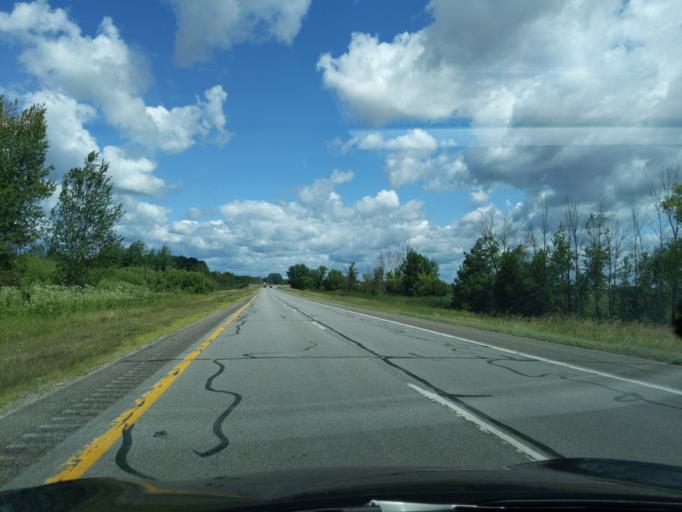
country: US
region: Michigan
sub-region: Clare County
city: Clare
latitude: 43.7569
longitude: -84.7575
